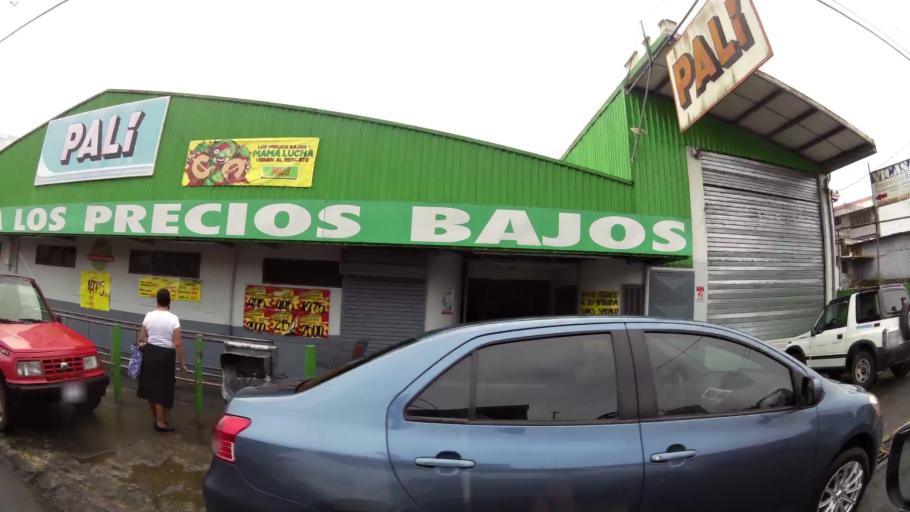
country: CR
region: Cartago
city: Paraiso
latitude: 9.8384
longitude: -83.8671
